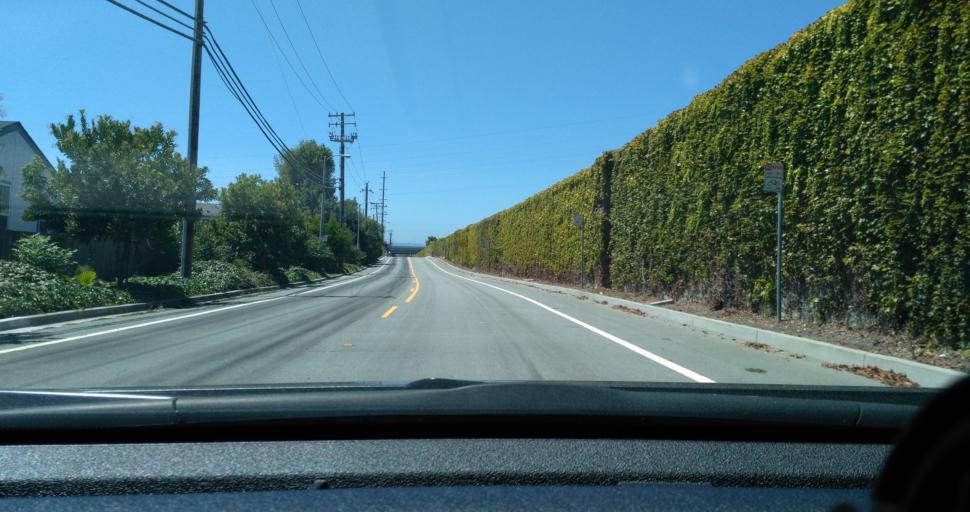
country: US
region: California
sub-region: Santa Clara County
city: Sunnyvale
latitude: 37.4079
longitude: -122.0040
